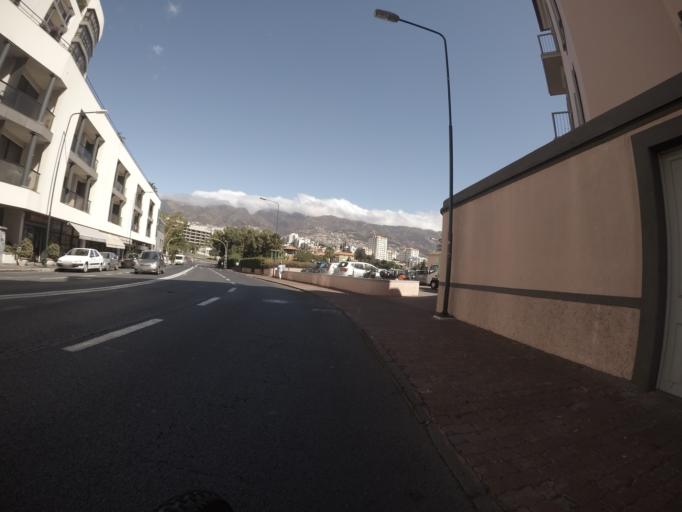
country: PT
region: Madeira
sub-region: Funchal
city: Funchal
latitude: 32.6410
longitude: -16.9240
